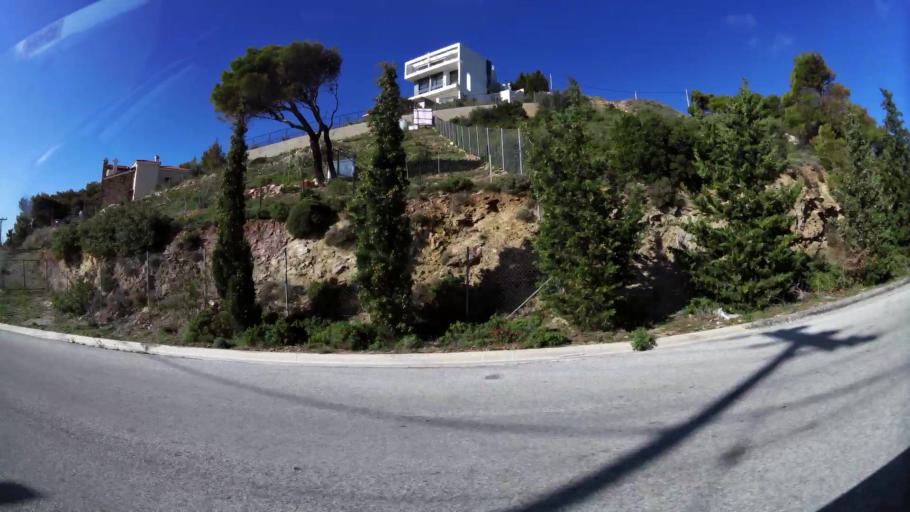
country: GR
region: Attica
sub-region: Nomarchia Anatolikis Attikis
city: Dhrafi
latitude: 38.0390
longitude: 23.8976
